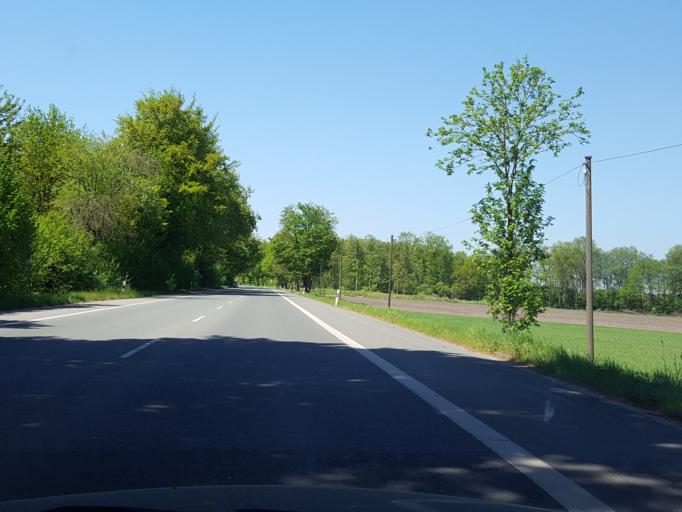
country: DE
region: North Rhine-Westphalia
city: Oer-Erkenschwick
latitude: 51.7082
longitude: 7.2914
